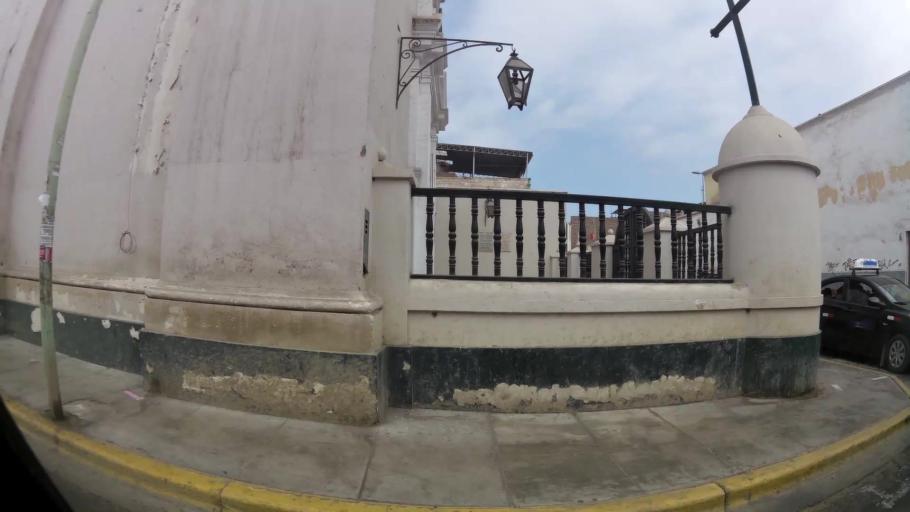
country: PE
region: La Libertad
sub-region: Provincia de Trujillo
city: Trujillo
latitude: -8.1057
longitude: -79.0259
